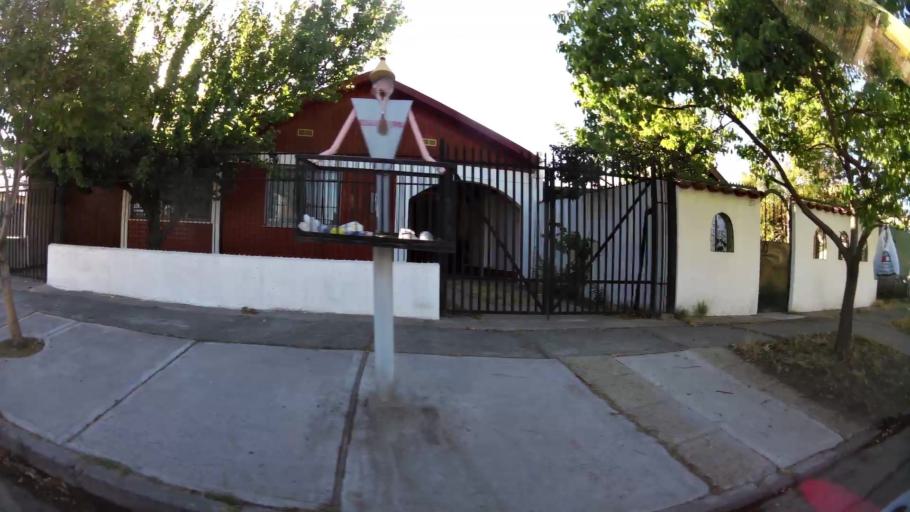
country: CL
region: O'Higgins
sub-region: Provincia de Cachapoal
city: Rancagua
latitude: -34.1713
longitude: -70.7188
